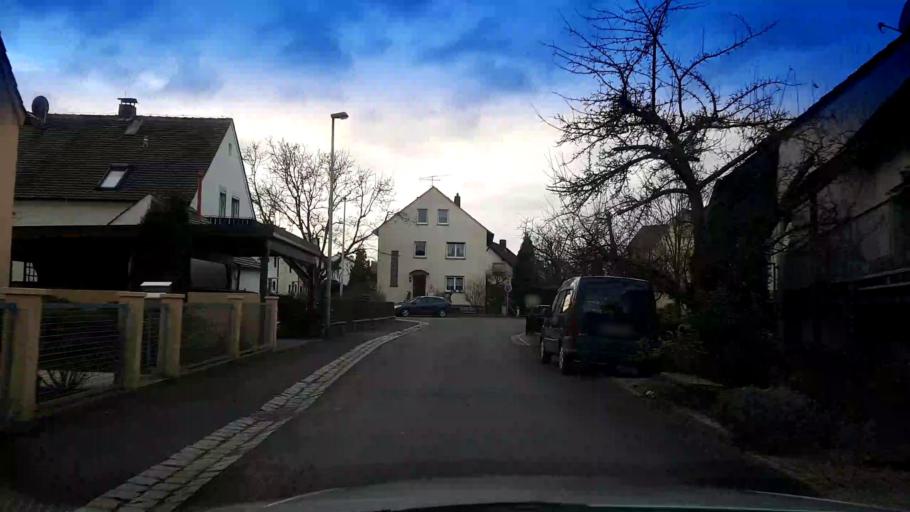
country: DE
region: Bavaria
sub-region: Upper Franconia
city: Gundelsheim
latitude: 49.9366
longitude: 10.9257
